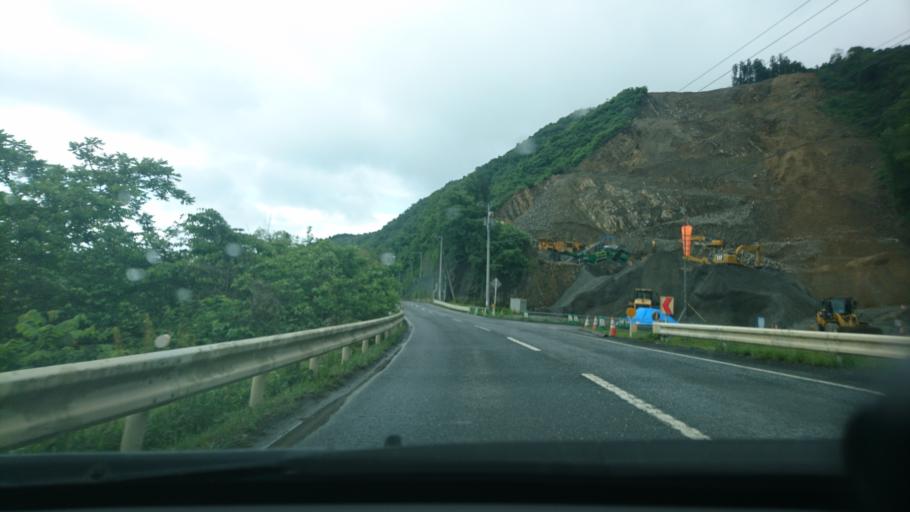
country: JP
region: Miyagi
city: Ishinomaki
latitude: 38.5554
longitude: 141.3078
